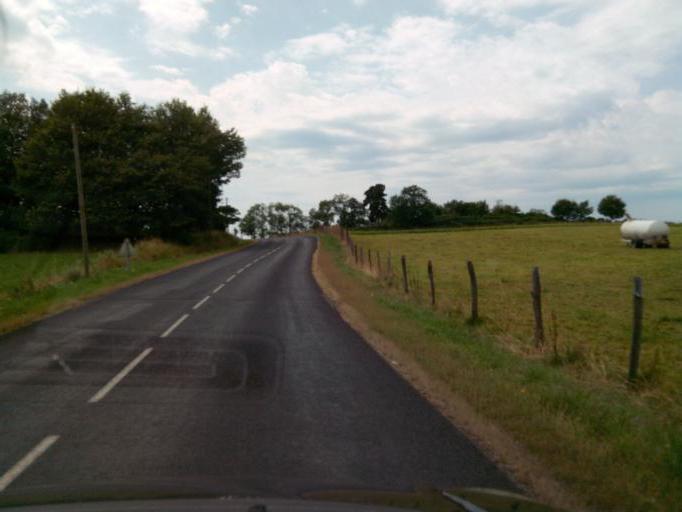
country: FR
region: Rhone-Alpes
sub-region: Departement de la Loire
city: Saint-Maurice-en-Gourgois
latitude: 45.3888
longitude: 4.1609
